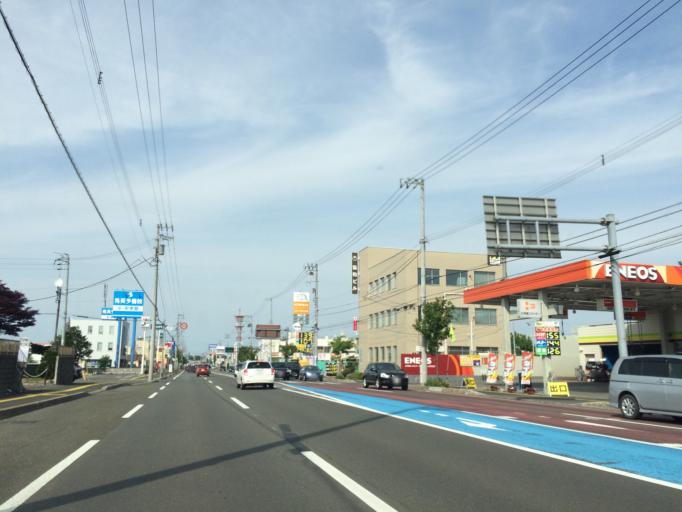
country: JP
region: Hokkaido
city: Ebetsu
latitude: 43.1056
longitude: 141.5413
